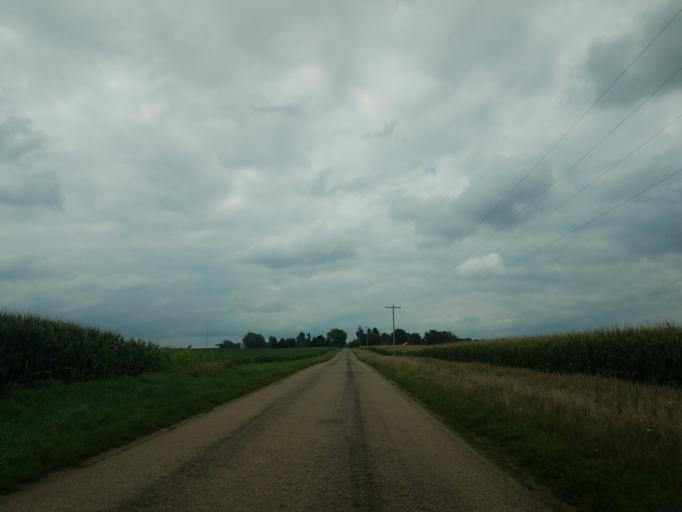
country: US
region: Illinois
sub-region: McLean County
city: Twin Grove
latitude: 40.4200
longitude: -89.0621
